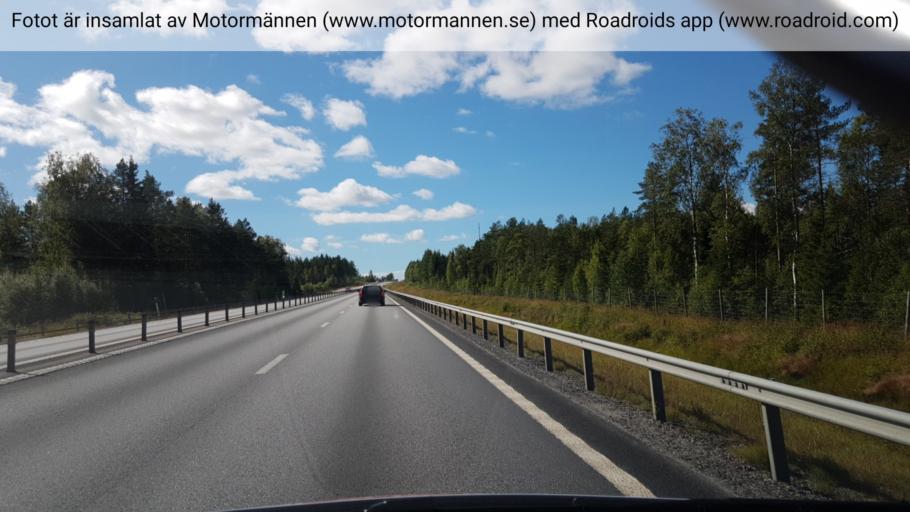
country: SE
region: Vaesterbotten
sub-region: Umea Kommun
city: Hoernefors
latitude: 63.6593
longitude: 19.9595
